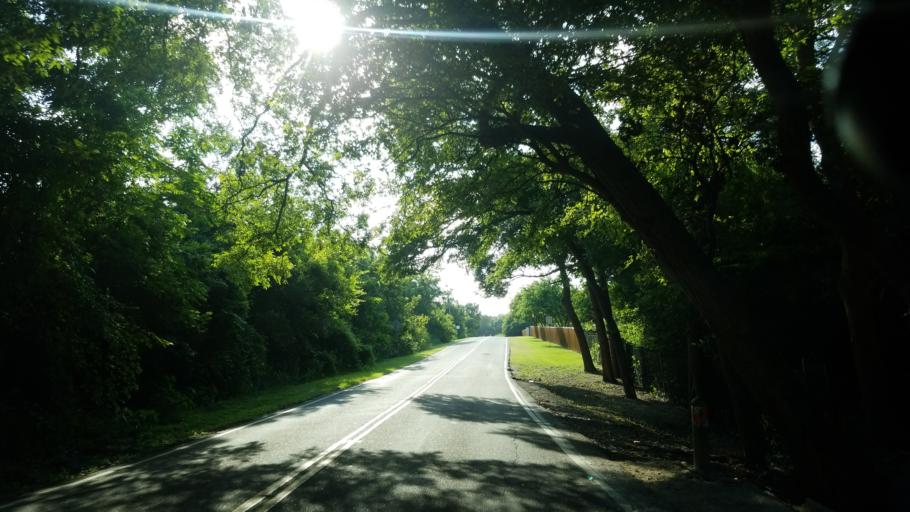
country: US
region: Texas
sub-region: Dallas County
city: Balch Springs
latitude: 32.7783
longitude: -96.7057
